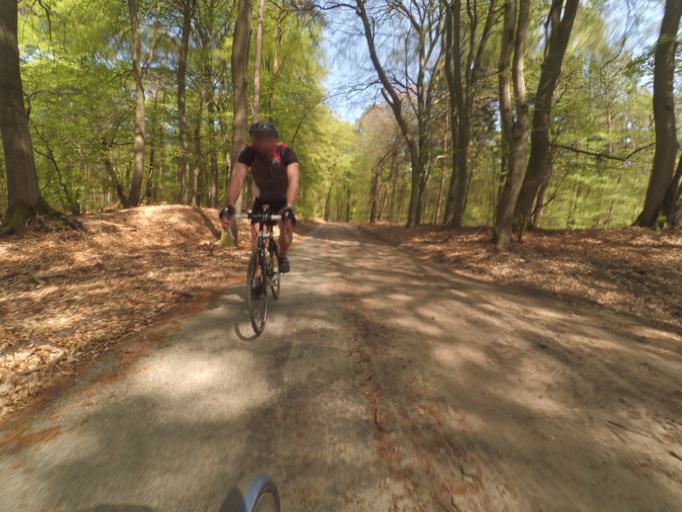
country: NL
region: Gelderland
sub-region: Gemeente Harderwijk
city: Harderwijk
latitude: 52.3238
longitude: 5.7026
